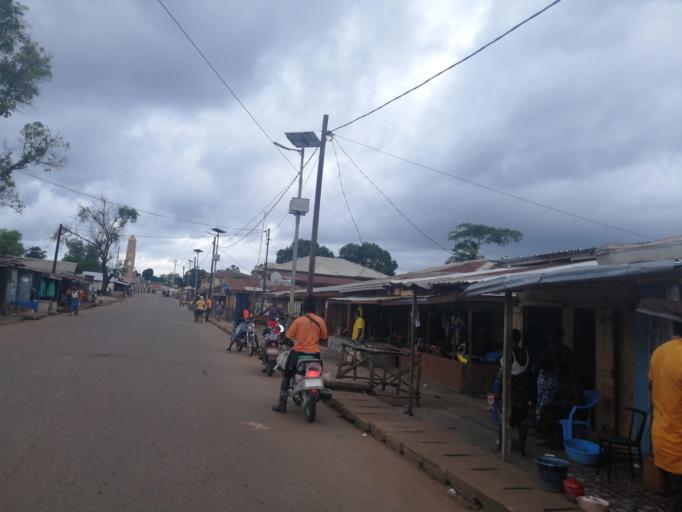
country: SL
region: Northern Province
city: Port Loko
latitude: 8.7650
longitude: -12.7876
